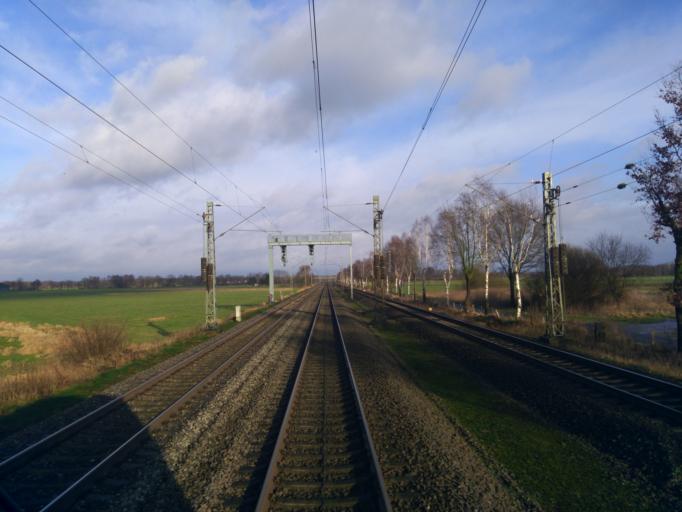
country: DE
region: Lower Saxony
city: Scheessel
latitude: 53.1754
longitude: 9.5099
